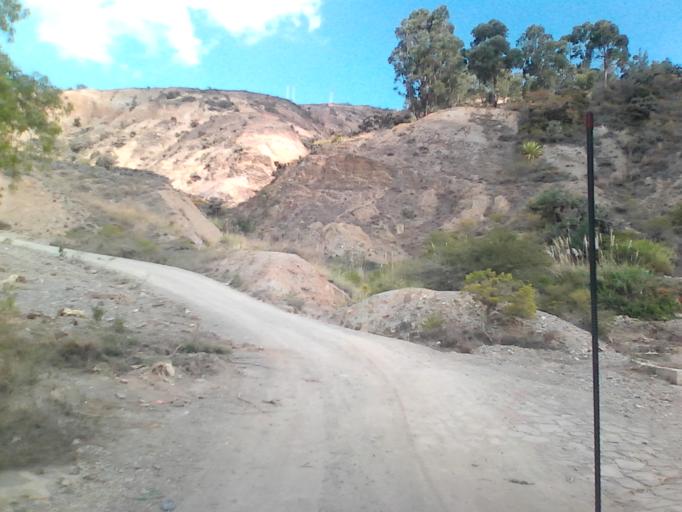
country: CO
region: Boyaca
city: Sachica
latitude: 5.5756
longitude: -73.5178
